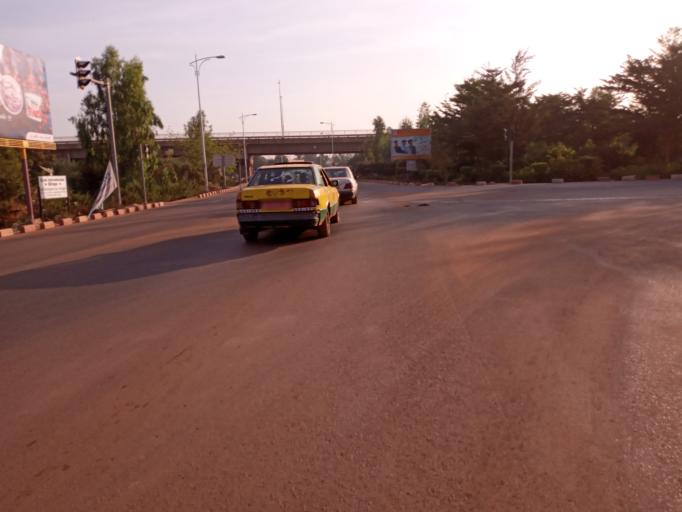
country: ML
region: Bamako
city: Bamako
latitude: 12.6360
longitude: -7.9243
